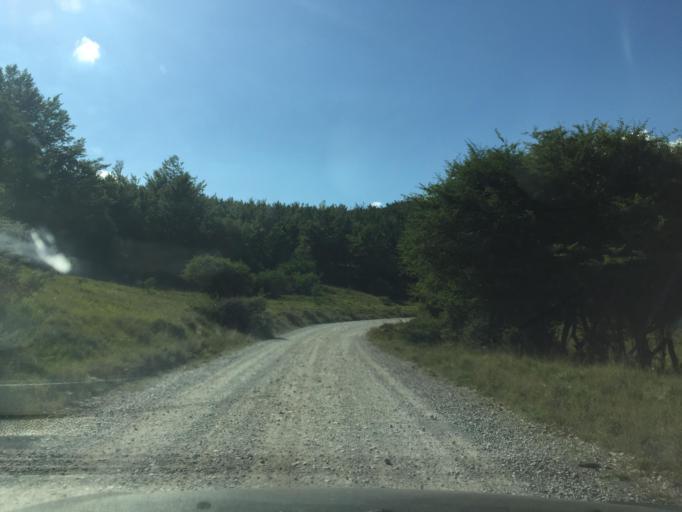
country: HR
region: Primorsko-Goranska
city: Klana
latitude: 45.4701
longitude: 14.4021
